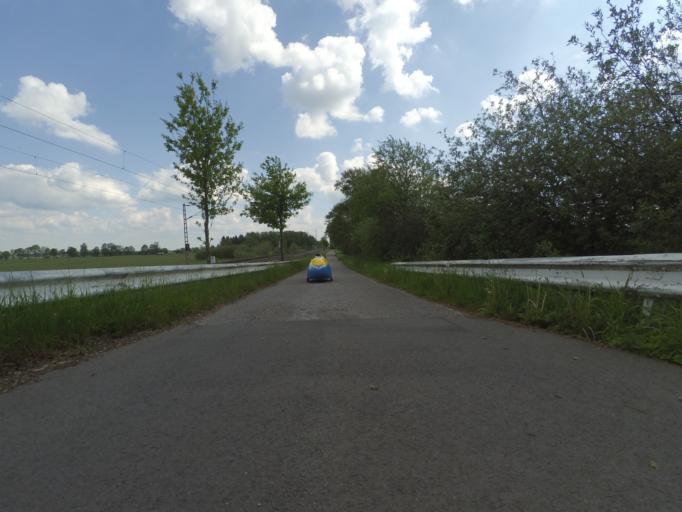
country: DE
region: Lower Saxony
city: Hambuhren
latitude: 52.5451
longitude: 9.9388
